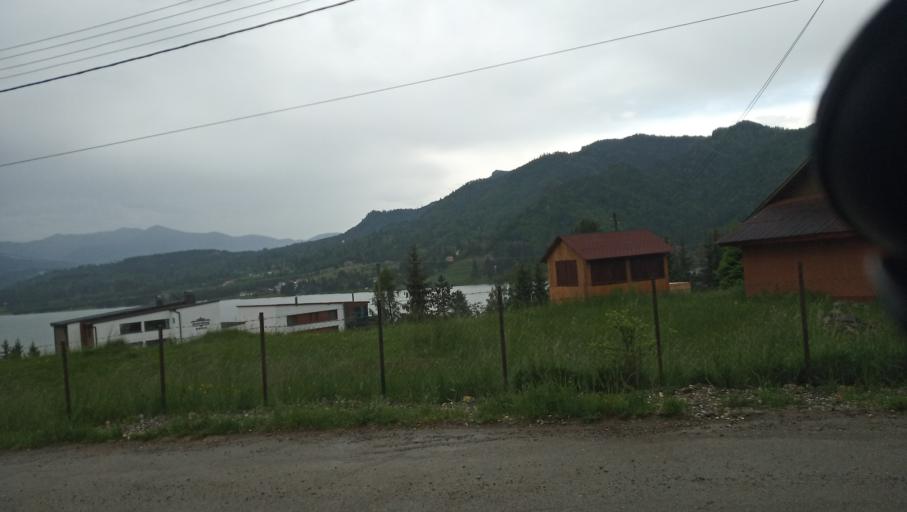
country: RO
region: Bistrita-Nasaud
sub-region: Comuna Tiha Bargaului
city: Tureac
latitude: 47.1710
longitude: 24.8858
